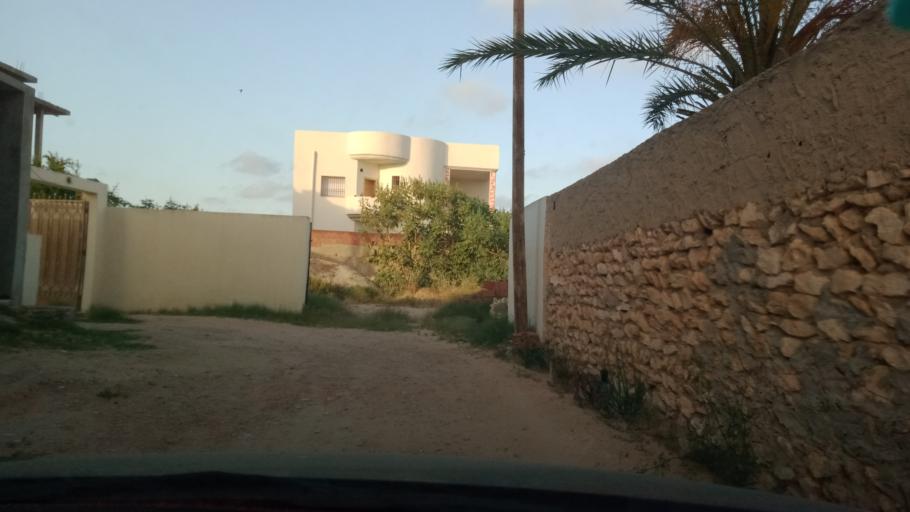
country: TN
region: Safaqis
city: Al Qarmadah
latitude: 34.8182
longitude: 10.7467
